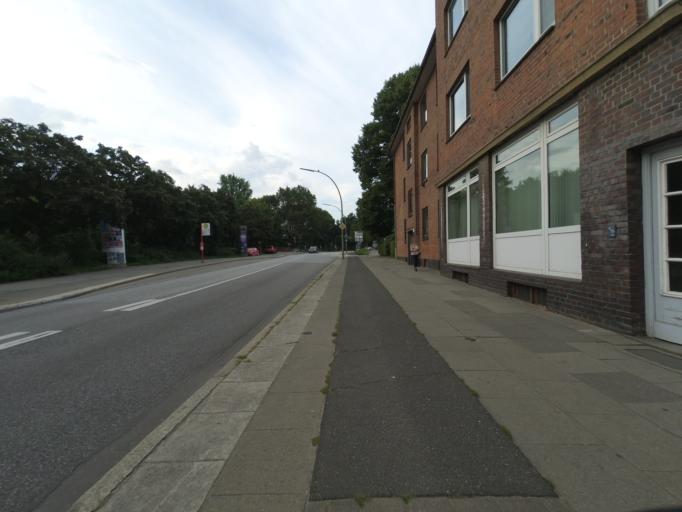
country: DE
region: Hamburg
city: Bergedorf
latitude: 53.4855
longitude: 10.2098
